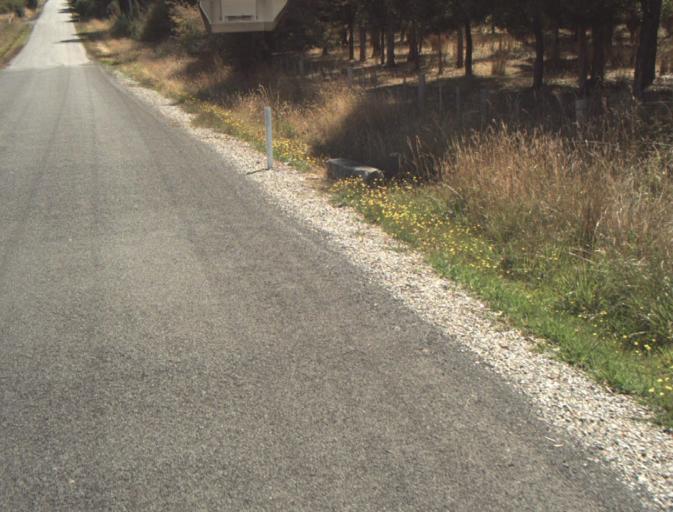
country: AU
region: Tasmania
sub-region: Launceston
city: Mayfield
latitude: -41.2376
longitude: 147.2339
